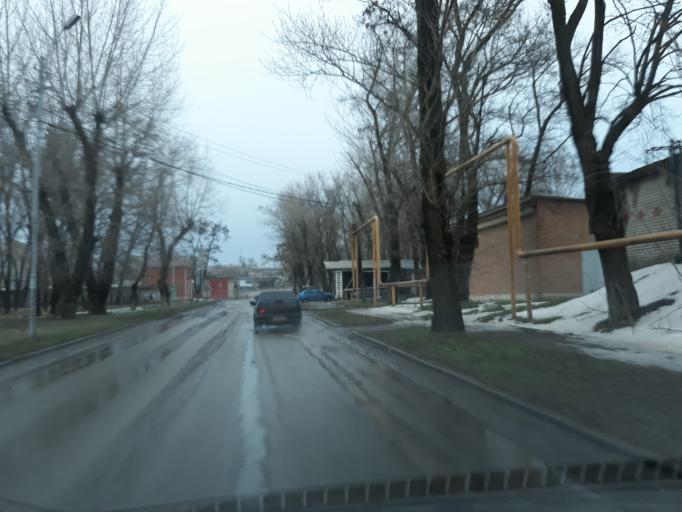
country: RU
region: Rostov
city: Taganrog
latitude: 47.2363
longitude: 38.9267
